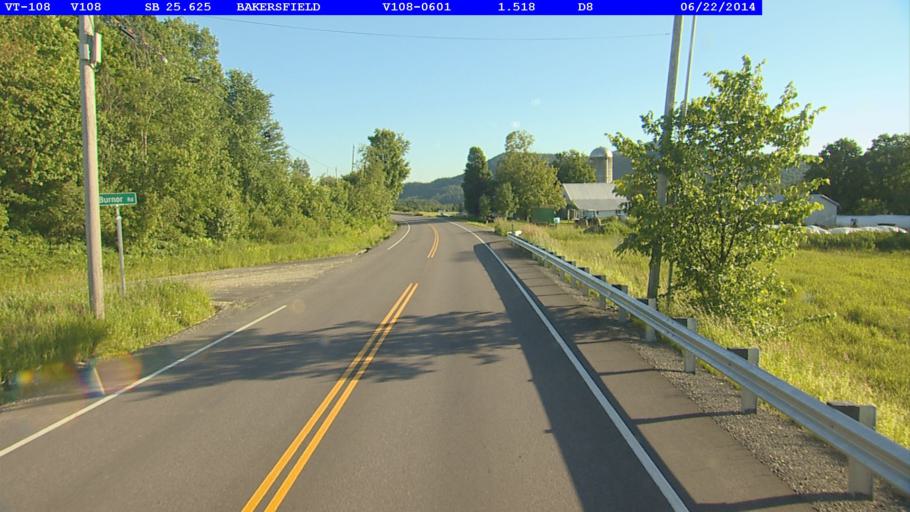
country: US
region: Vermont
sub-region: Franklin County
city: Enosburg Falls
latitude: 44.7548
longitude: -72.8215
